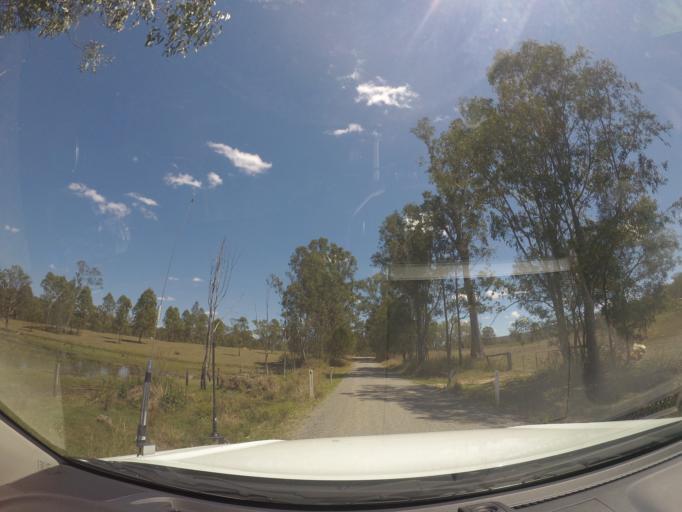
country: AU
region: Queensland
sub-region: Logan
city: Cedar Vale
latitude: -27.8460
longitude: 152.8815
